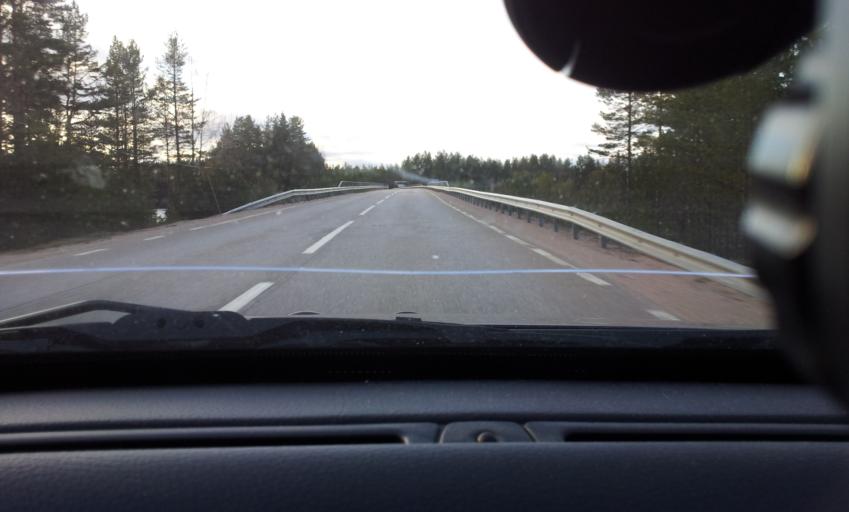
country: SE
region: Jaemtland
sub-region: Harjedalens Kommun
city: Sveg
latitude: 62.1212
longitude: 15.0375
